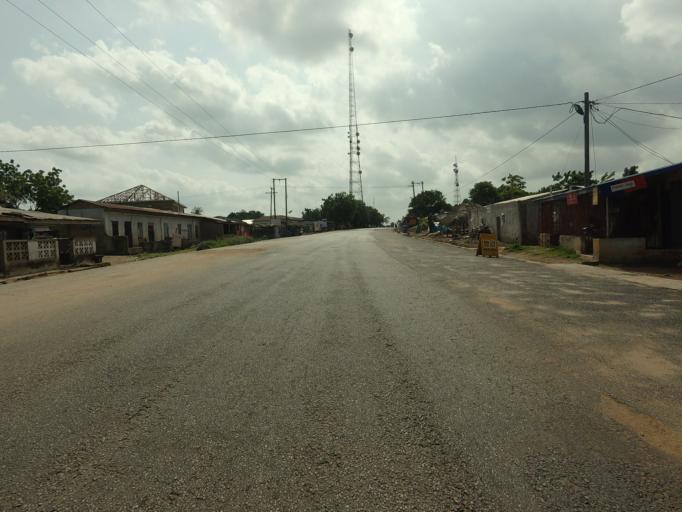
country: GH
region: Volta
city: Ho
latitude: 6.4159
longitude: 0.7458
